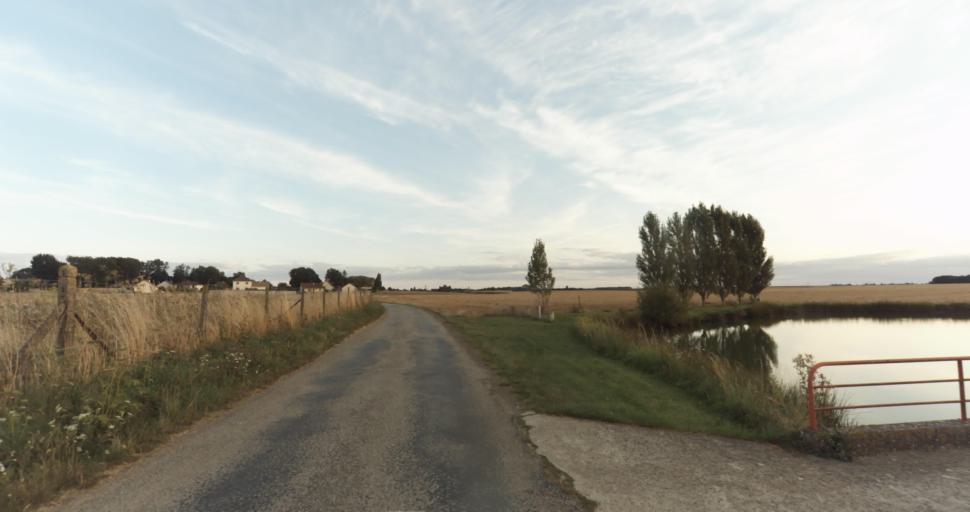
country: FR
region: Haute-Normandie
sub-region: Departement de l'Eure
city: La Madeleine-de-Nonancourt
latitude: 48.8971
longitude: 1.2344
